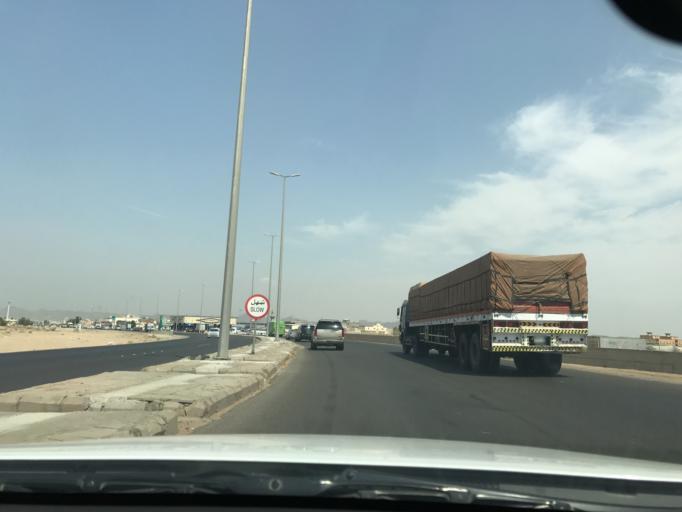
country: SA
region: Makkah
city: Jeddah
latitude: 21.3993
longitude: 39.4338
